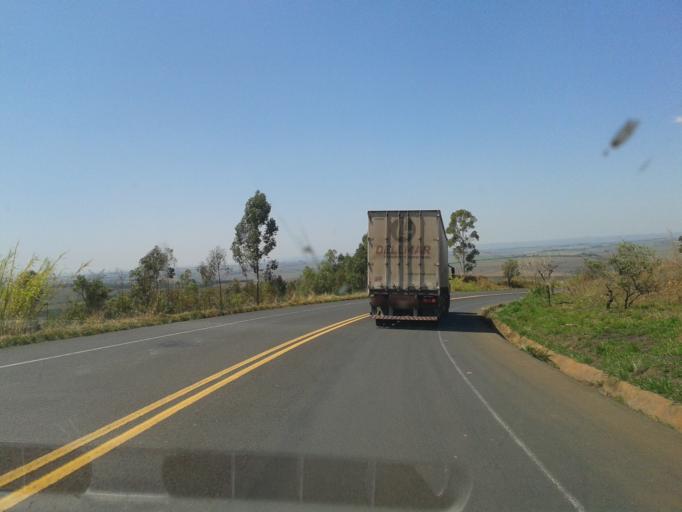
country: BR
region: Minas Gerais
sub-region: Araxa
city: Araxa
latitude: -19.4244
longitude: -47.2364
